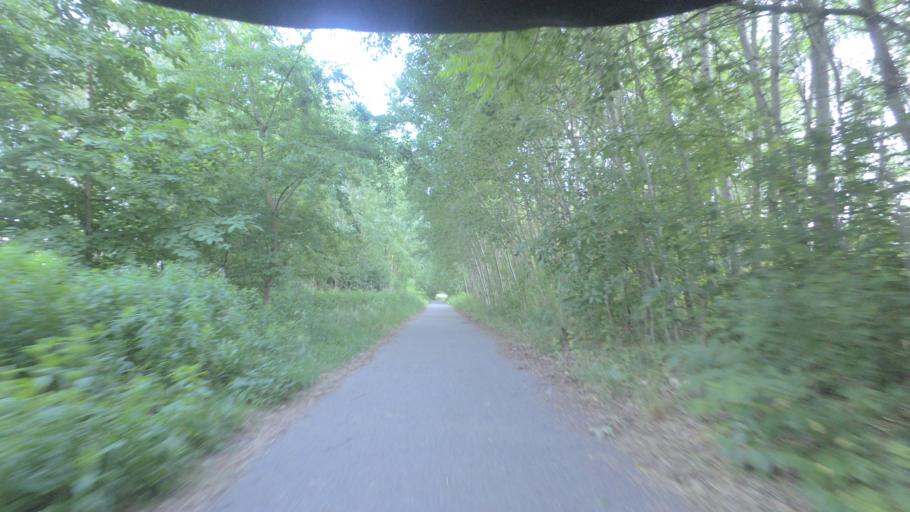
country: DE
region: Berlin
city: Lichtenrade
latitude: 52.3885
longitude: 13.4274
